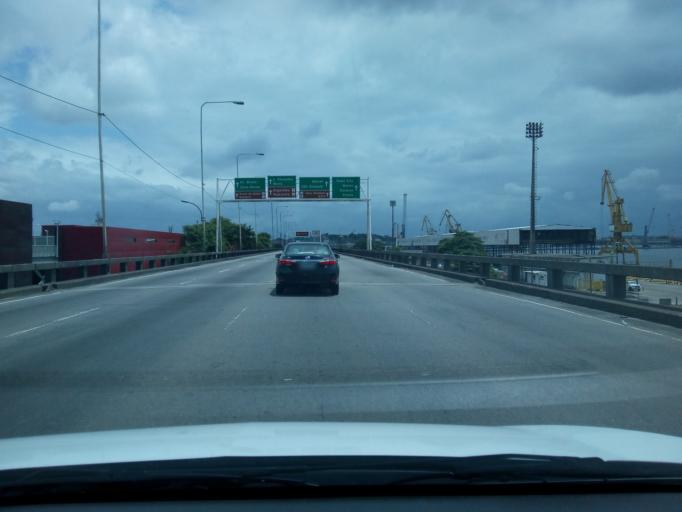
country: BR
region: Rio de Janeiro
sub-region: Rio De Janeiro
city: Rio de Janeiro
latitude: -22.8943
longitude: -43.2138
